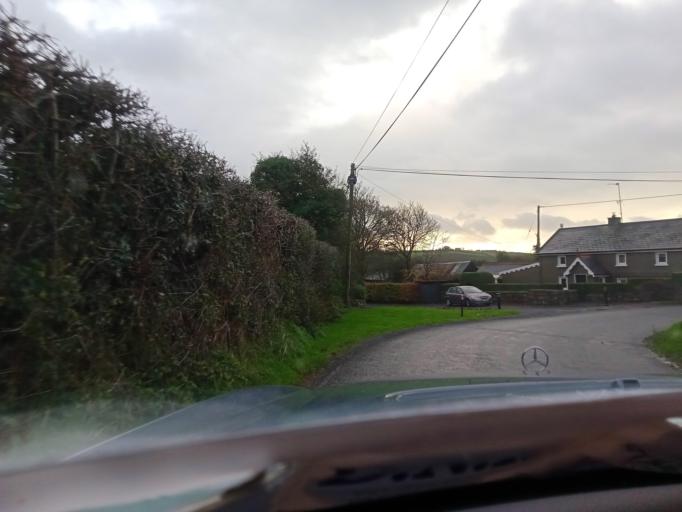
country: IE
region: Munster
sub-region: Waterford
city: Waterford
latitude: 52.2751
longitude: -7.1788
